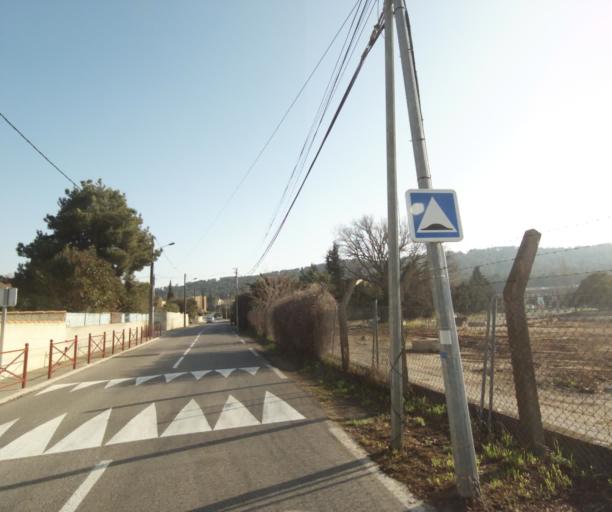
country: FR
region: Provence-Alpes-Cote d'Azur
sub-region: Departement des Bouches-du-Rhone
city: Les Pennes-Mirabeau
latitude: 43.4169
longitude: 5.2989
